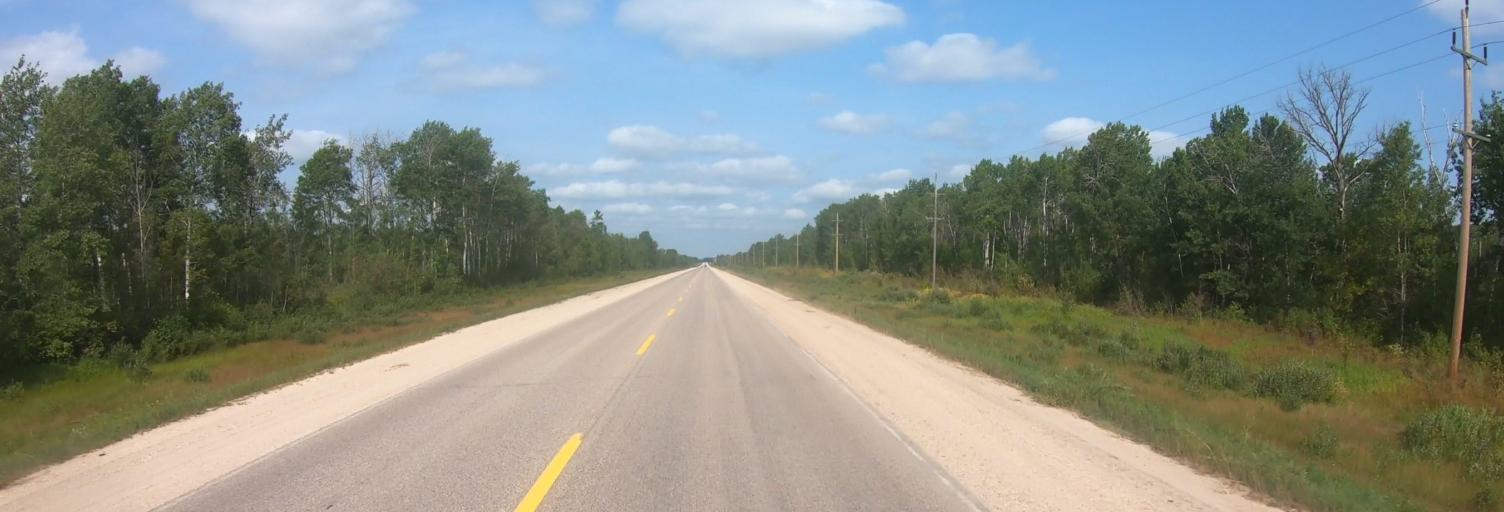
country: CA
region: Manitoba
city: La Broquerie
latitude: 49.1994
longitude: -96.2700
